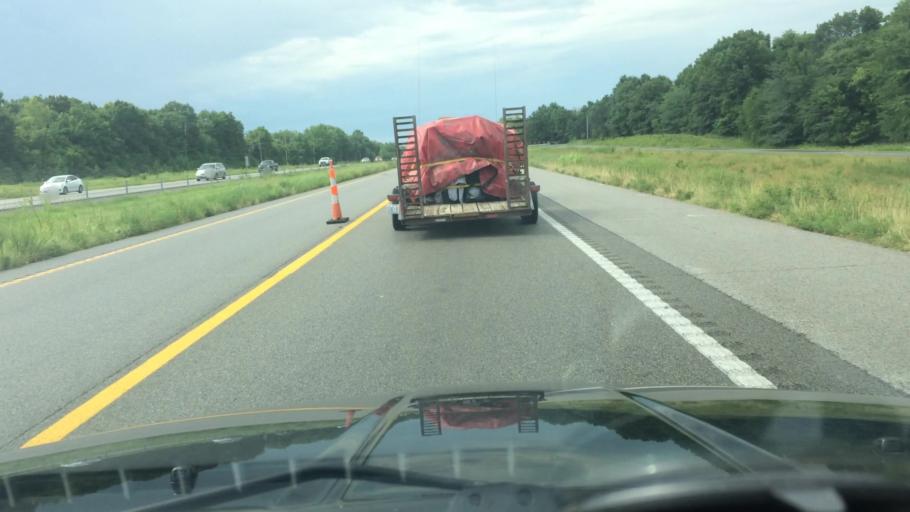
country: US
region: Missouri
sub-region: Cass County
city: Peculiar
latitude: 38.6848
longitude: -94.4235
